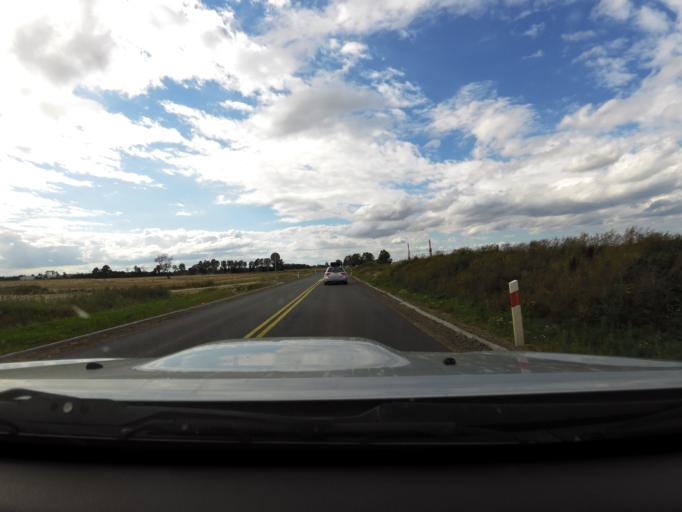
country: PL
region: Pomeranian Voivodeship
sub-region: Powiat gdanski
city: Cedry Wielkie
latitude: 54.2886
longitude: 18.8324
